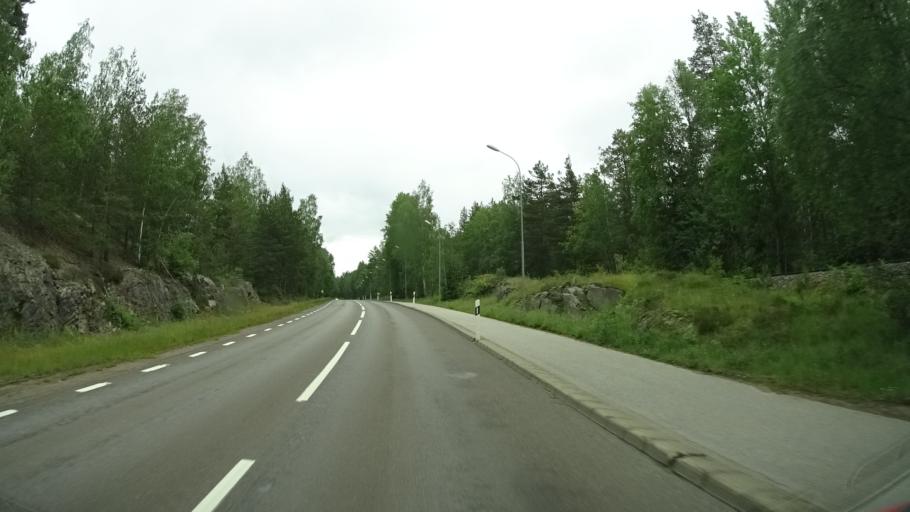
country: SE
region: Kalmar
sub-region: Hultsfreds Kommun
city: Hultsfred
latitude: 57.5479
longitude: 15.7278
